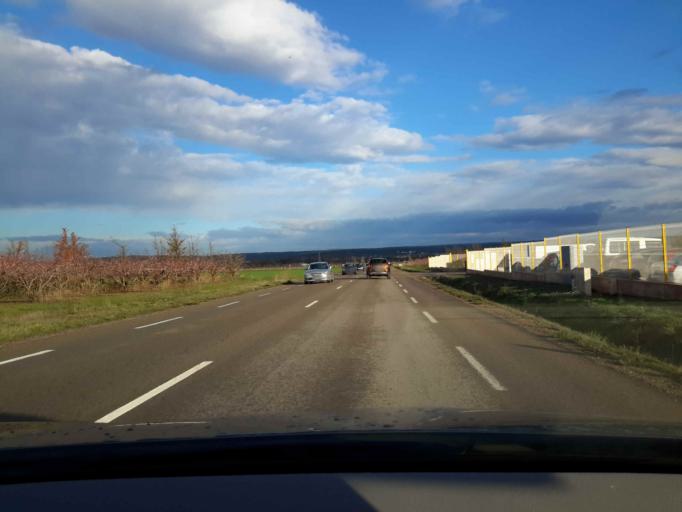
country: FR
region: Languedoc-Roussillon
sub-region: Departement du Gard
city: Aubord
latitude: 43.7598
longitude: 4.3364
